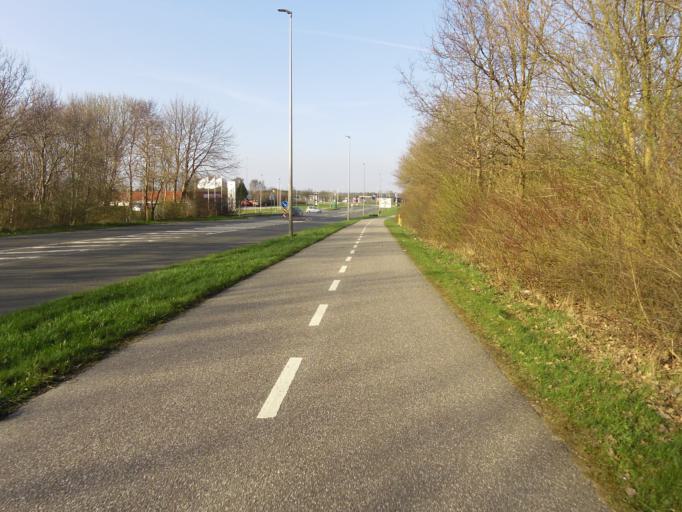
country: DK
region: South Denmark
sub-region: Vejen Kommune
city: Vejen
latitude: 55.4874
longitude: 9.1280
